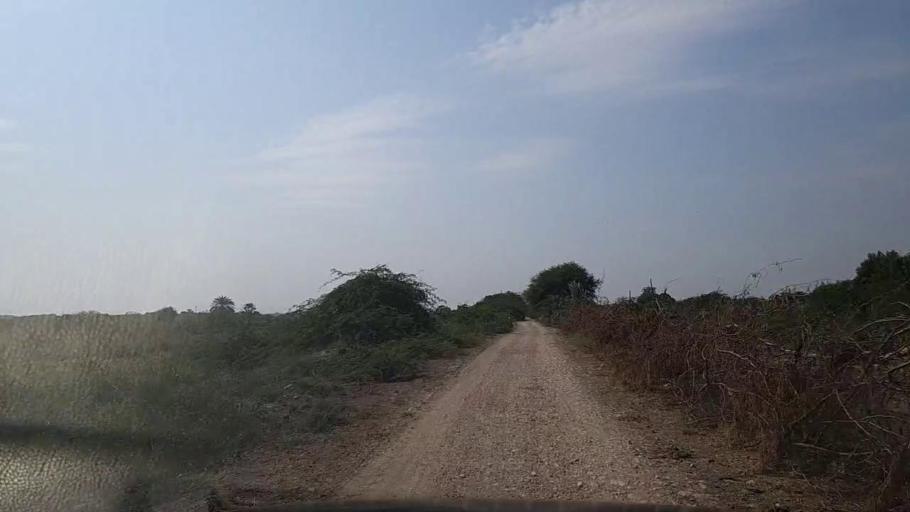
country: PK
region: Sindh
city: Thatta
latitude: 24.7697
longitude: 67.8087
